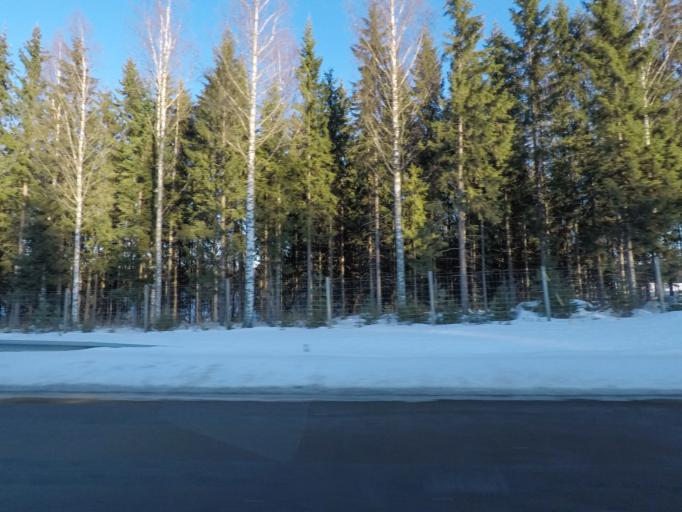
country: FI
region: Paijanne Tavastia
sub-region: Lahti
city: Lahti
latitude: 60.8715
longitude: 25.5747
